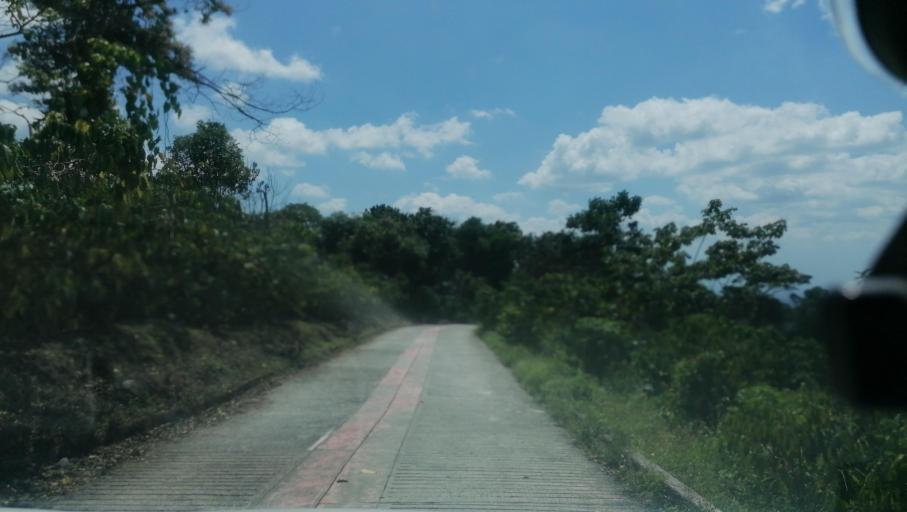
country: MX
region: Chiapas
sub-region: Cacahoatan
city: Benito Juarez
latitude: 15.0469
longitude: -92.1480
